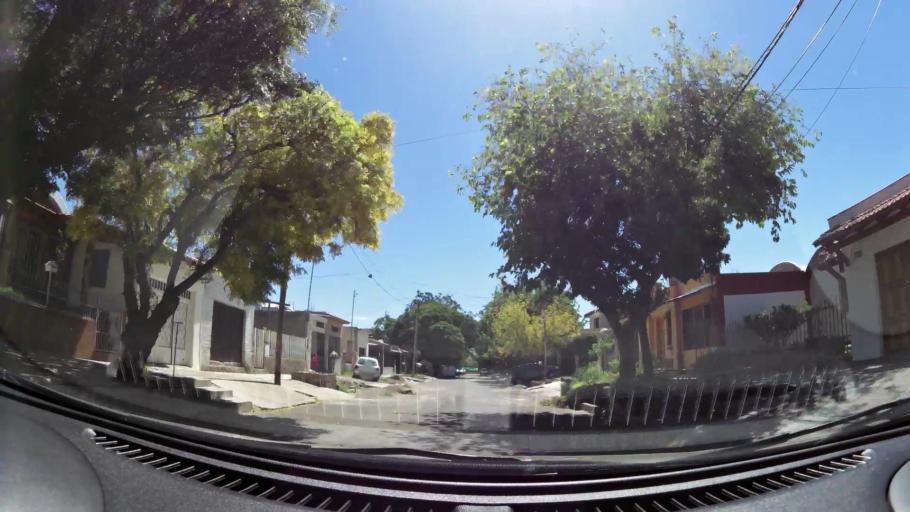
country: AR
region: Mendoza
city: Las Heras
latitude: -32.8392
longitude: -68.8716
